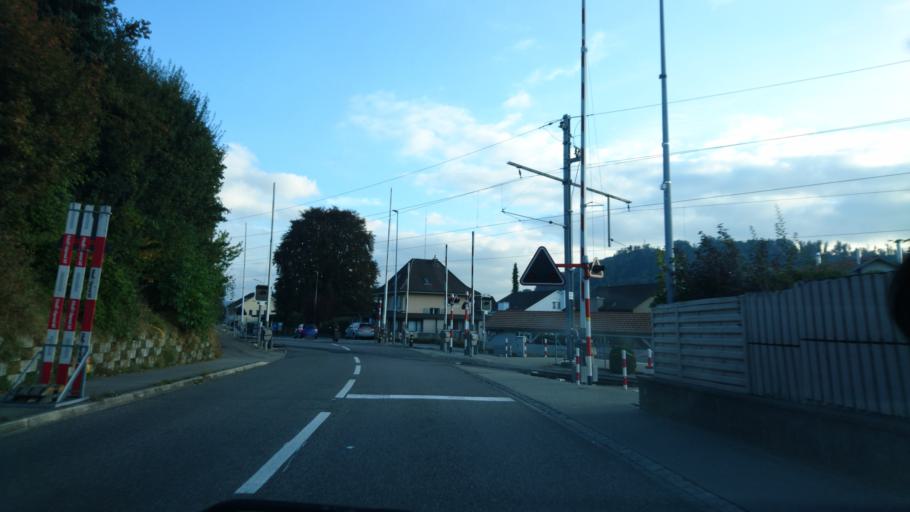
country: CH
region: Bern
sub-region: Bern-Mittelland District
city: Vechigen
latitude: 46.9533
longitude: 7.5486
